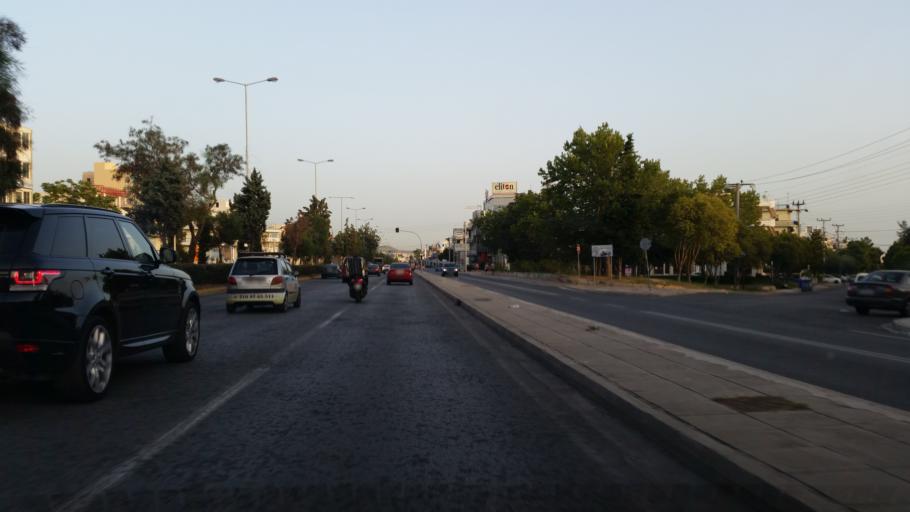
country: GR
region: Attica
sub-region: Nomarchia Athinas
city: Elliniko
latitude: 37.8835
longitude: 23.7522
